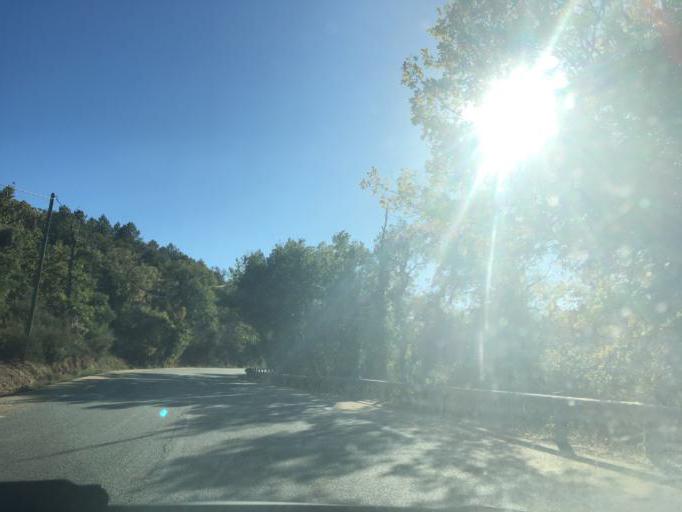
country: FR
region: Provence-Alpes-Cote d'Azur
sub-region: Departement du Var
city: La Garde-Freinet
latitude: 43.3013
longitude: 6.4809
